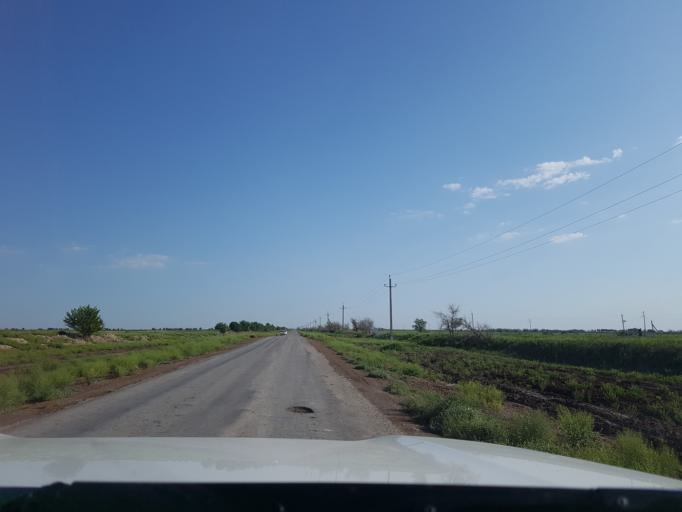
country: TM
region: Dasoguz
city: Koeneuergench
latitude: 41.8476
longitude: 58.7048
